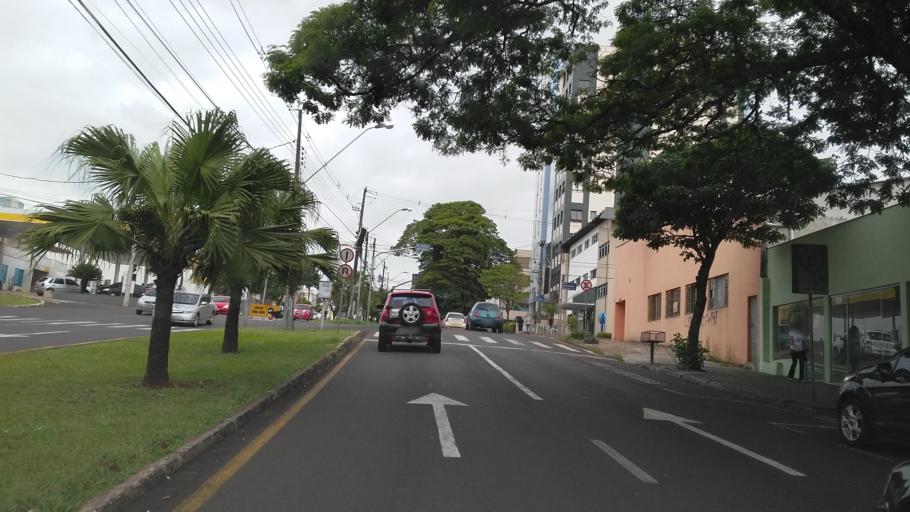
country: BR
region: Parana
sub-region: Londrina
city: Londrina
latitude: -23.3198
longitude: -51.1545
